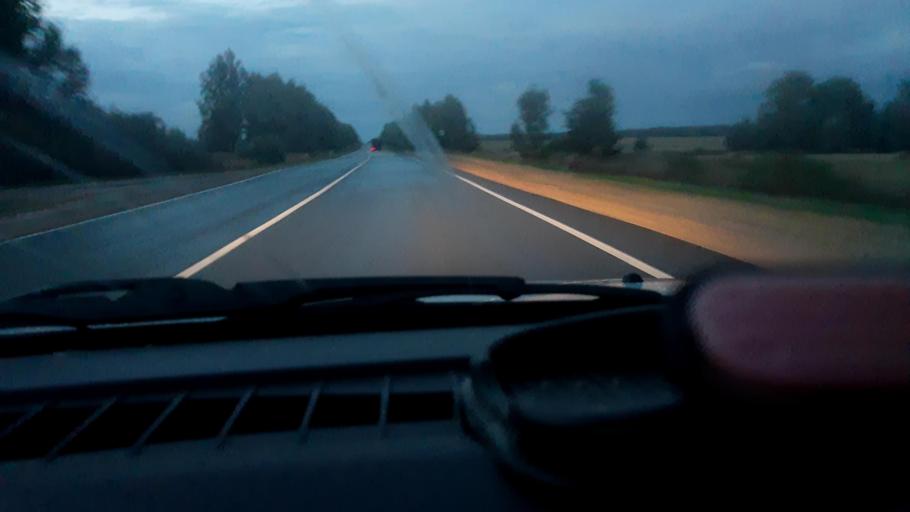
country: RU
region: Nizjnij Novgorod
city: Vladimirskoye
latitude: 56.9142
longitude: 45.0512
